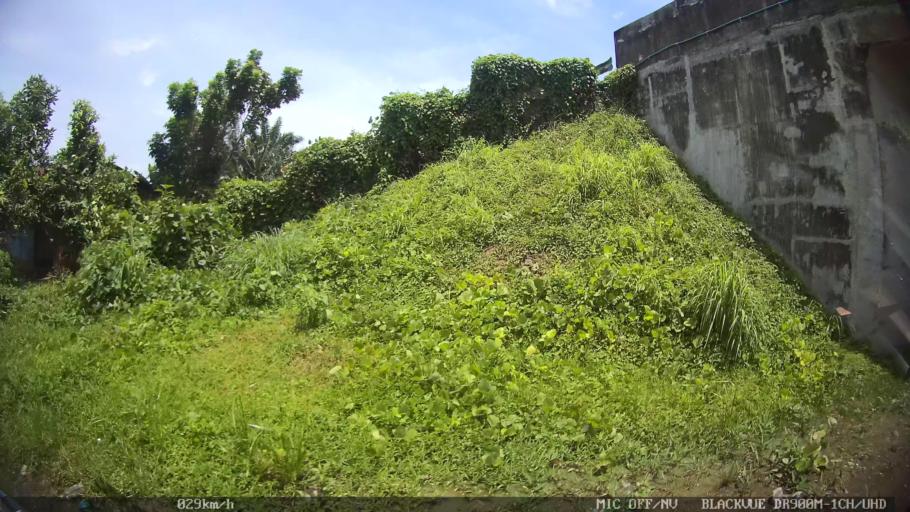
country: ID
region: North Sumatra
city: Percut
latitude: 3.5496
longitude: 98.8519
